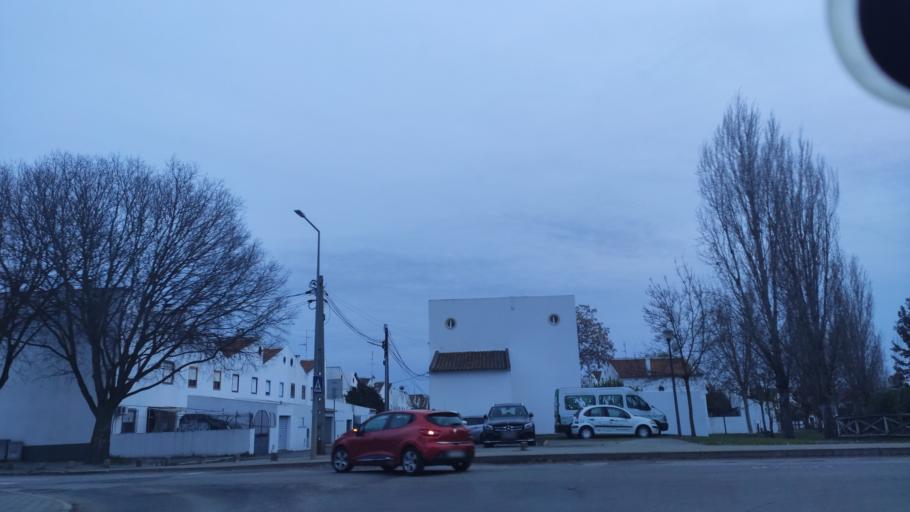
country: PT
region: Beja
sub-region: Beja
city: Beja
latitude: 38.0195
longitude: -7.8523
